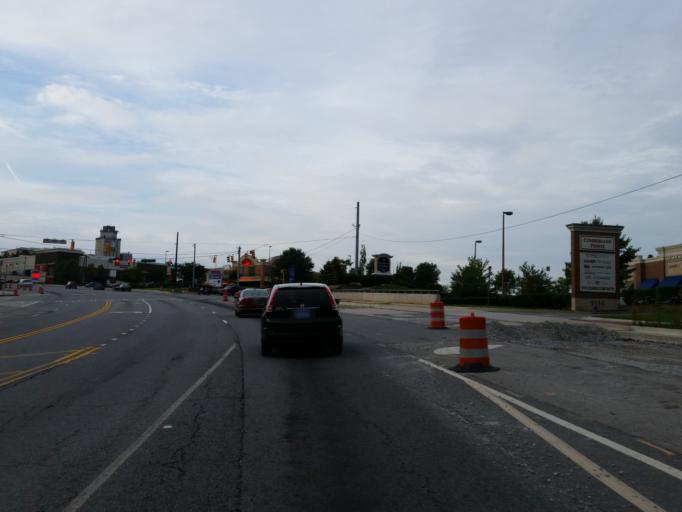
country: US
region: Georgia
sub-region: Cobb County
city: Vinings
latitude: 33.8757
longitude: -84.4559
